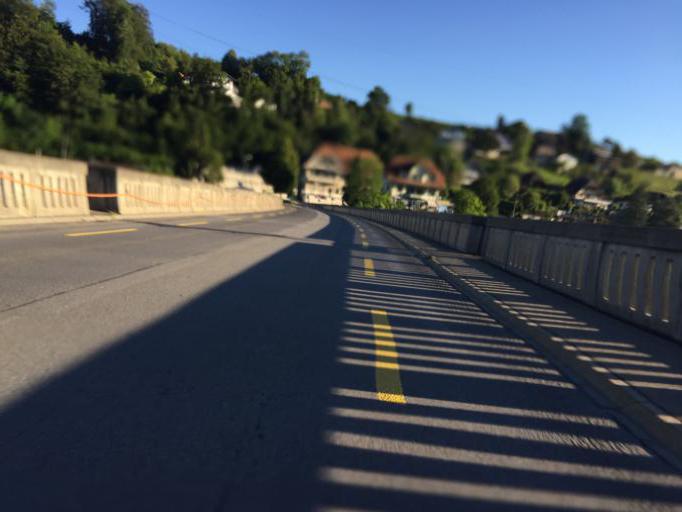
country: CH
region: Bern
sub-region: Bern-Mittelland District
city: Kirchlindach
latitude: 46.9715
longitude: 7.4184
